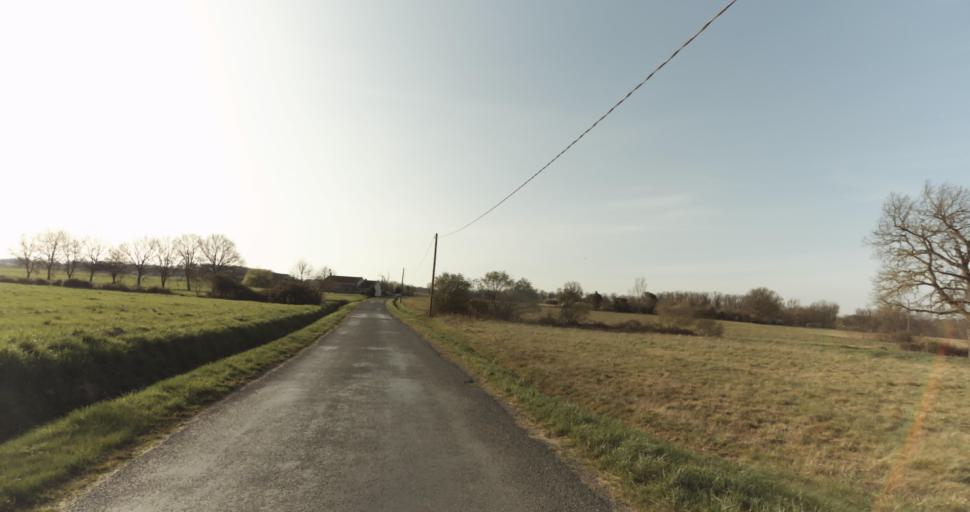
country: FR
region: Midi-Pyrenees
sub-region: Departement du Tarn
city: Saint-Sulpice-la-Pointe
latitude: 43.7436
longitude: 1.6874
